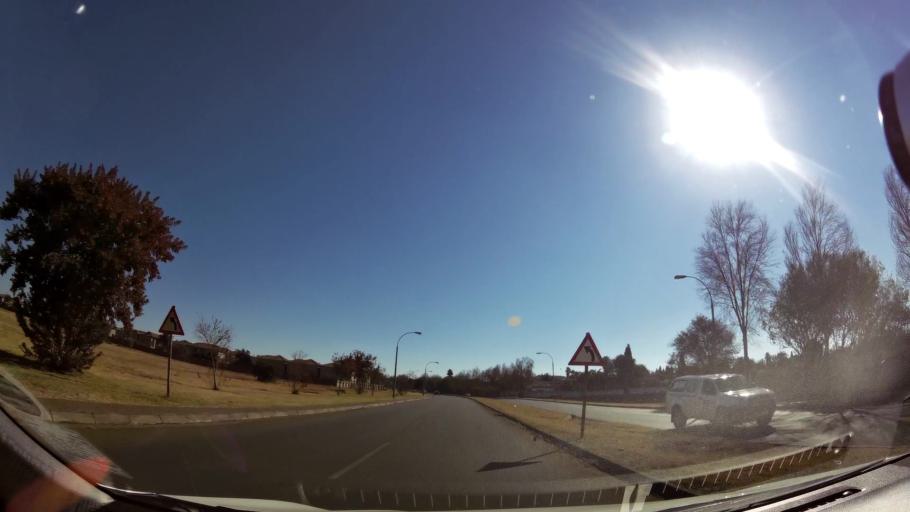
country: ZA
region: Gauteng
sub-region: Ekurhuleni Metropolitan Municipality
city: Germiston
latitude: -26.3031
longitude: 28.0952
